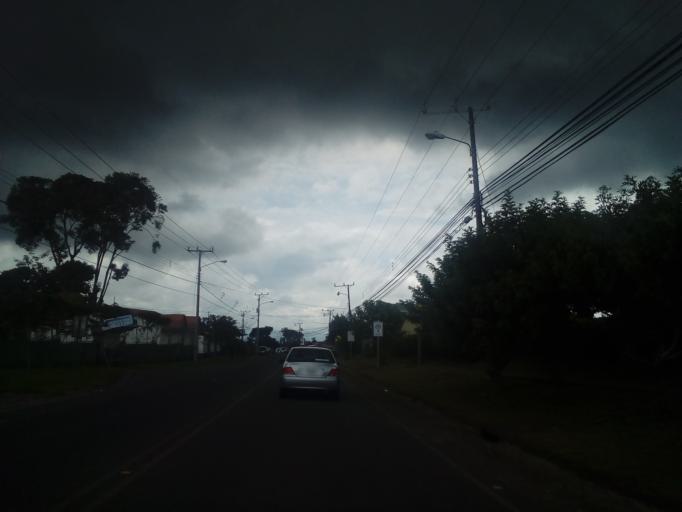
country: CR
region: Heredia
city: Angeles
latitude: 9.9914
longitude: -84.0564
